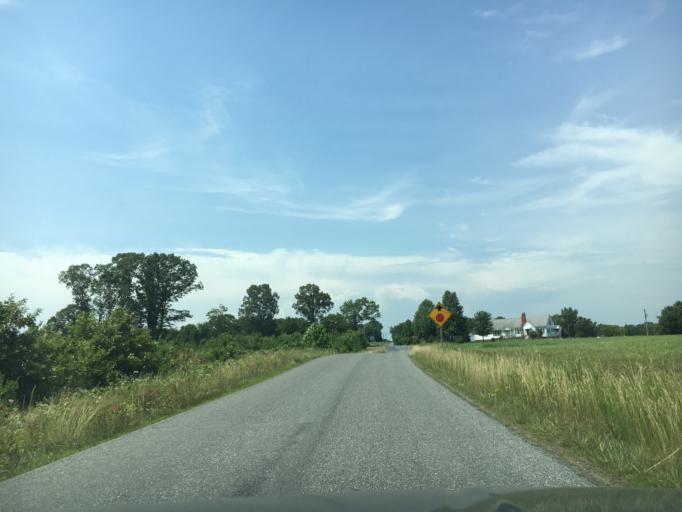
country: US
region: Virginia
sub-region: Pittsylvania County
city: Chatham
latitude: 36.8890
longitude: -79.4059
